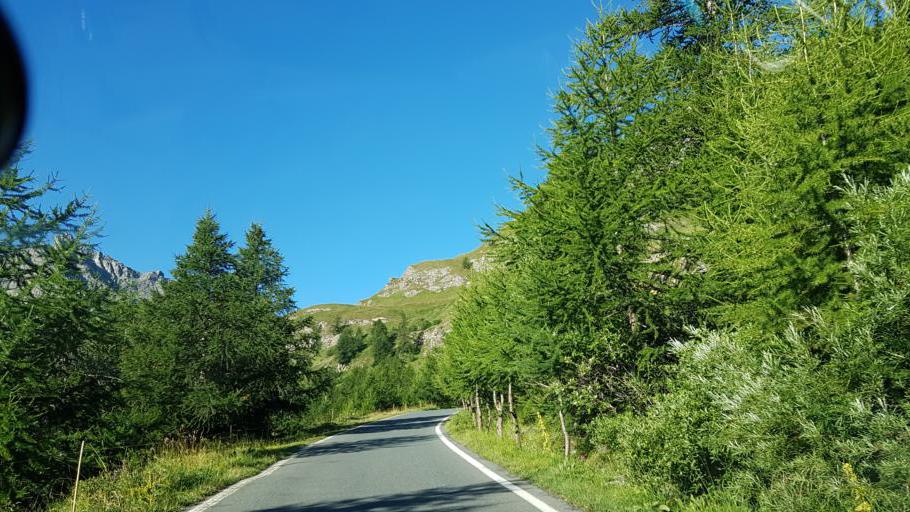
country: IT
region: Piedmont
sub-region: Provincia di Cuneo
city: Pontechianale
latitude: 44.6611
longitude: 6.9902
